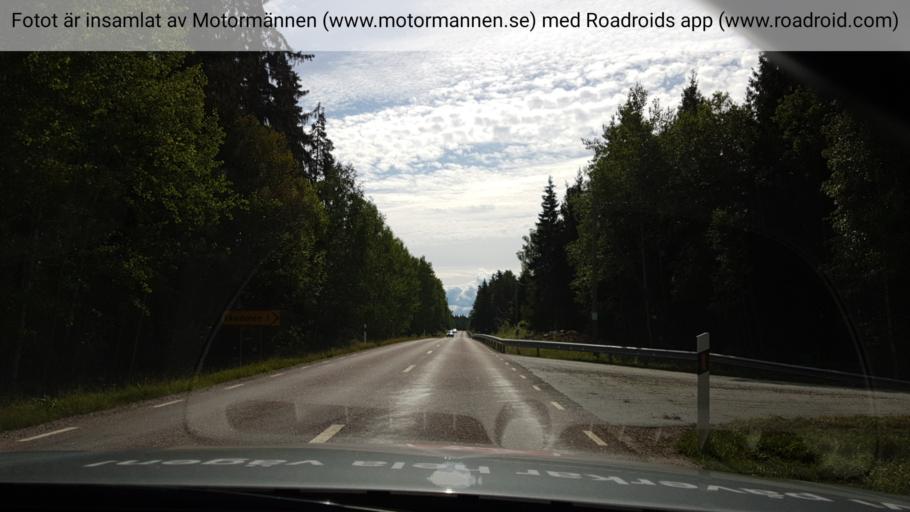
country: SE
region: Uppsala
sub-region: Heby Kommun
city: OEstervala
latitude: 59.9973
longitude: 17.3115
